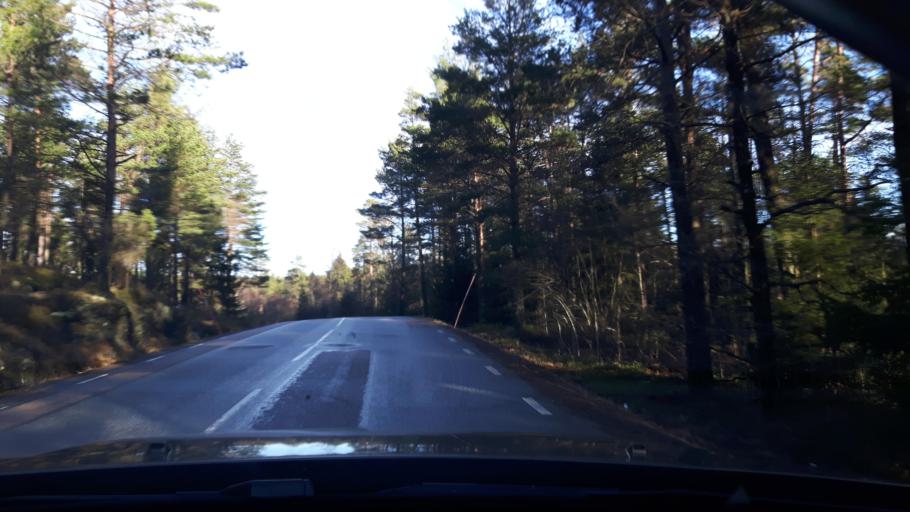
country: SE
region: Vaestra Goetaland
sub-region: Munkedals Kommun
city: Munkedal
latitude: 58.5071
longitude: 11.6817
